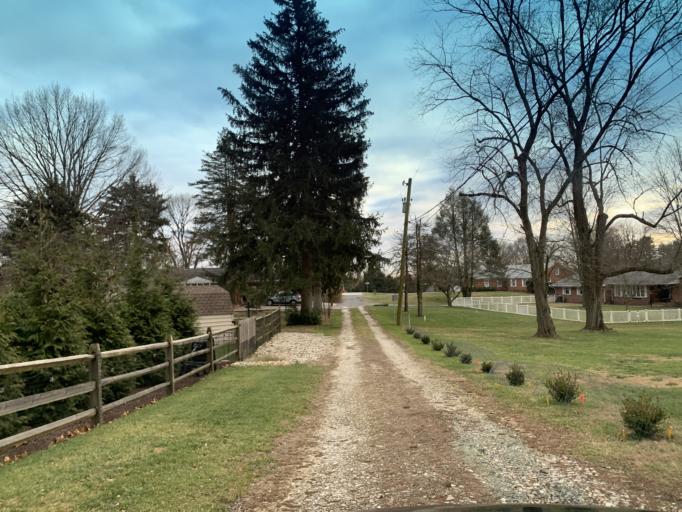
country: US
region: Maryland
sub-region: Baltimore County
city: Perry Hall
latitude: 39.4279
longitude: -76.4586
